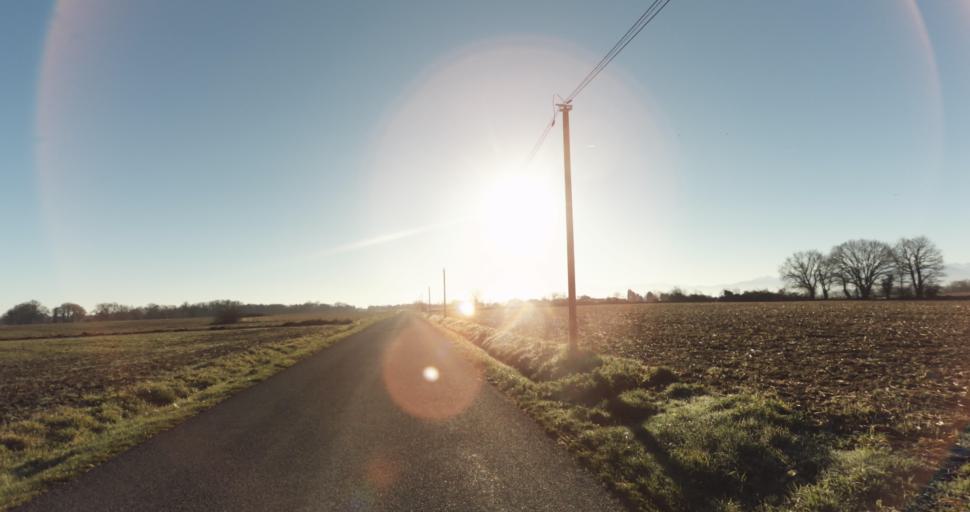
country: FR
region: Aquitaine
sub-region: Departement des Pyrenees-Atlantiques
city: Morlaas
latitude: 43.3203
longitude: -0.2479
